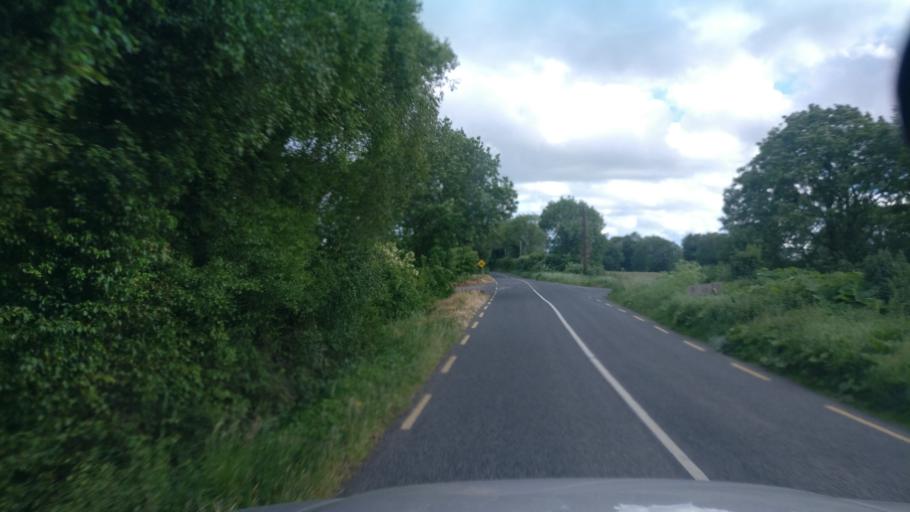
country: IE
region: Connaught
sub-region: County Galway
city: Portumna
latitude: 53.1965
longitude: -8.3032
